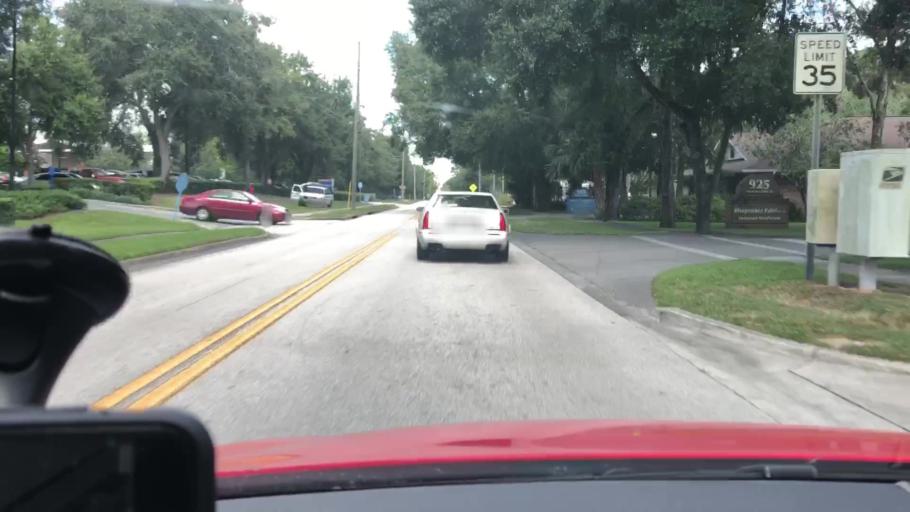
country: US
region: Florida
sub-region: Volusia County
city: North DeLand
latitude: 29.0431
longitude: -81.3163
